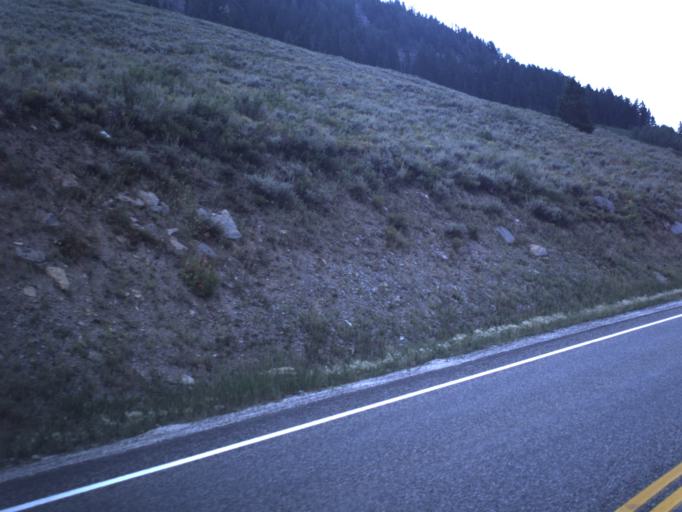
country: US
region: Idaho
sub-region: Bear Lake County
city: Paris
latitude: 41.9410
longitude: -111.4817
